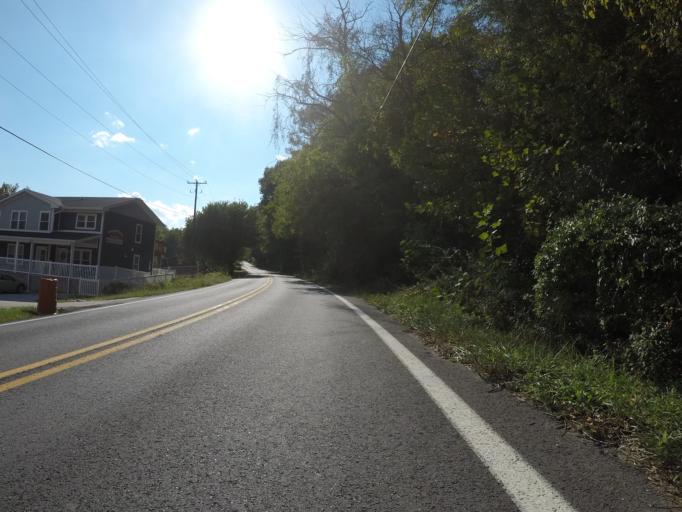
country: US
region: Ohio
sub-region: Lawrence County
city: Burlington
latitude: 38.3628
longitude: -82.5102
